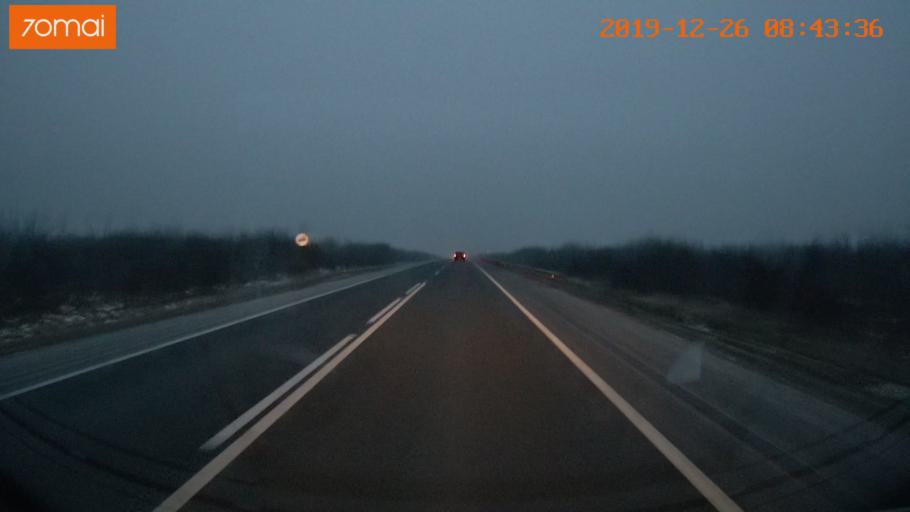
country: RU
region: Jaroslavl
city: Prechistoye
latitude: 58.5749
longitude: 40.3527
